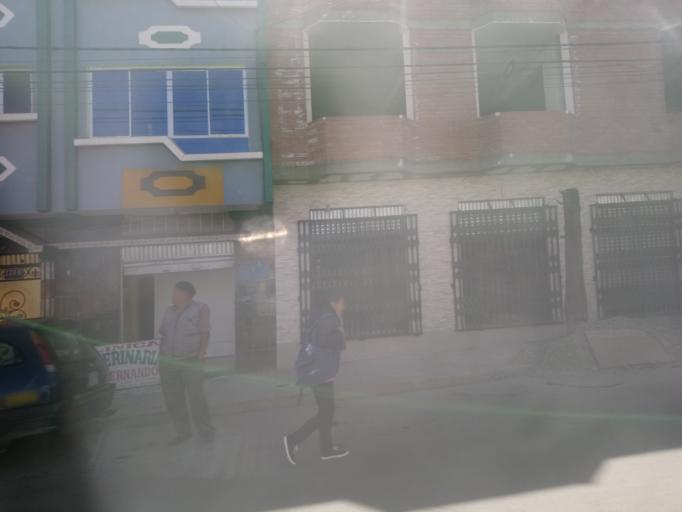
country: BO
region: La Paz
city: La Paz
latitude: -16.5001
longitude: -68.1054
